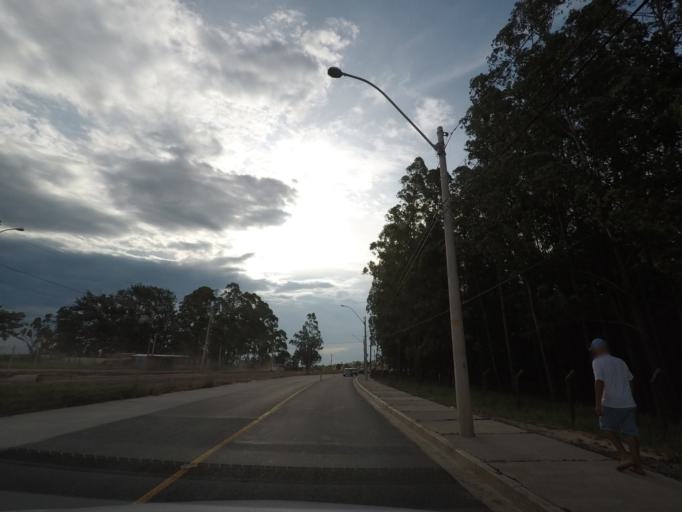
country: BR
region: Sao Paulo
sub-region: Hortolandia
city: Hortolandia
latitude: -22.9428
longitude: -47.1766
